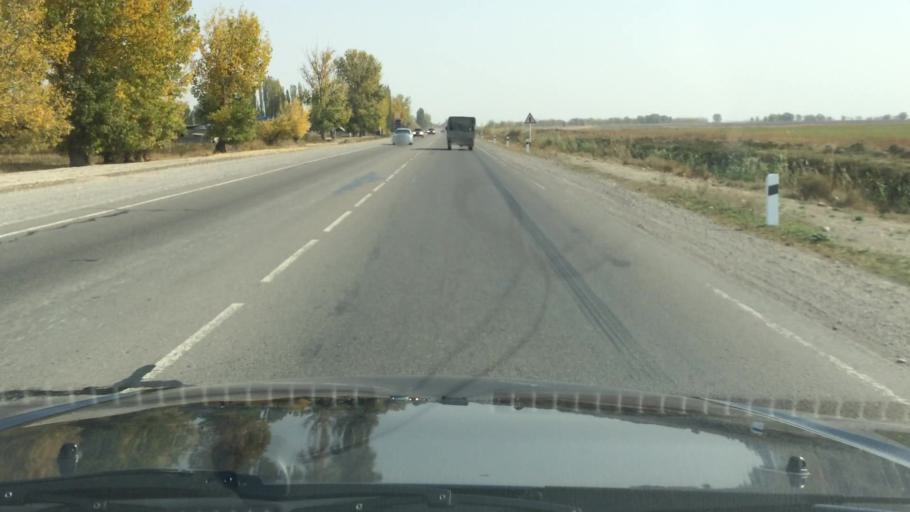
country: KG
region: Chuy
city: Lebedinovka
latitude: 42.9212
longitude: 74.7401
